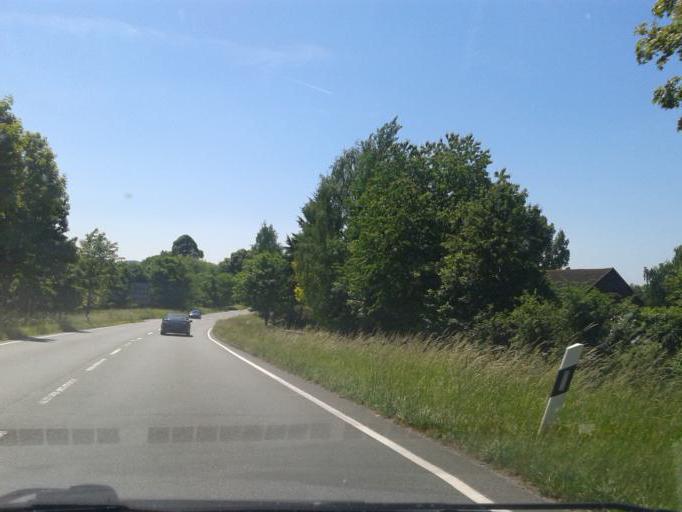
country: DE
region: North Rhine-Westphalia
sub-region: Regierungsbezirk Detmold
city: Blomberg
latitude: 51.9367
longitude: 9.0796
